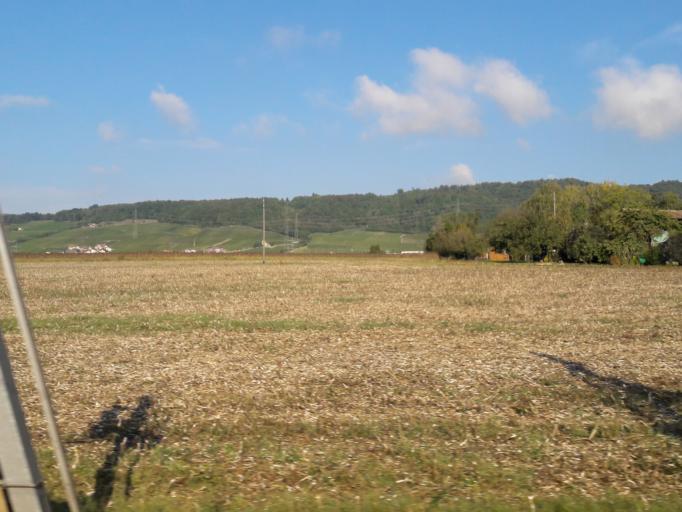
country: CH
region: Vaud
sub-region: Nyon District
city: Gland
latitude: 46.4379
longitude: 6.2882
